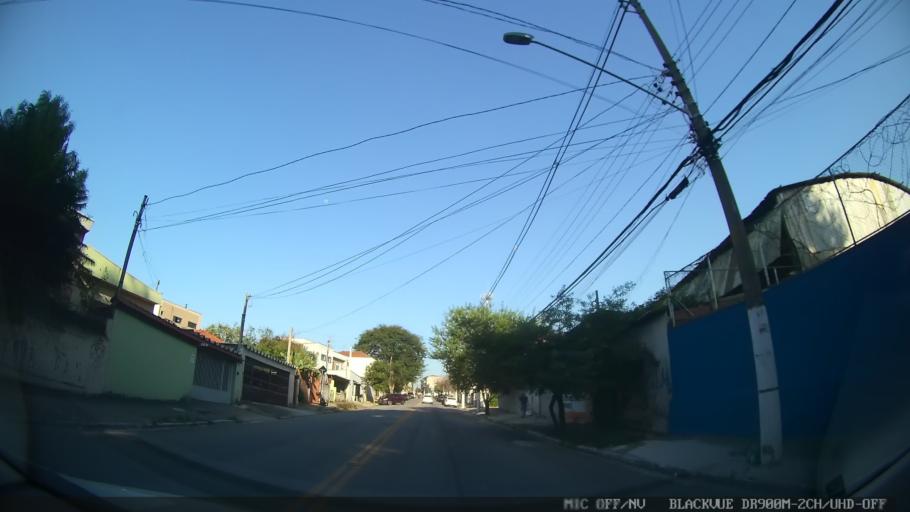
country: BR
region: Sao Paulo
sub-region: Sao Paulo
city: Sao Paulo
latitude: -23.4918
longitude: -46.6509
